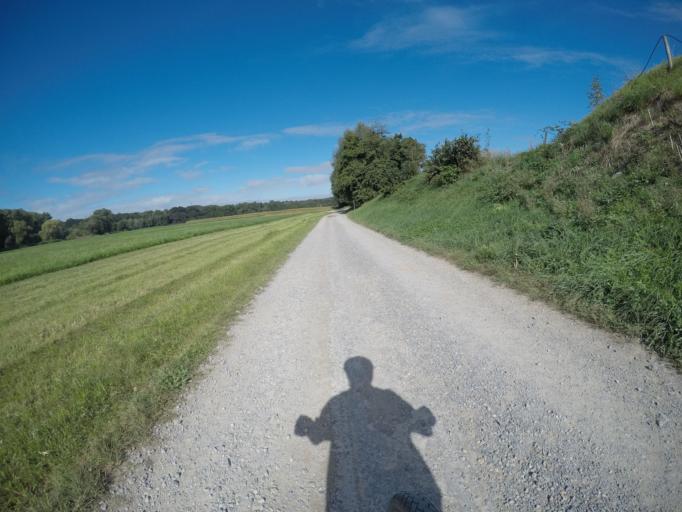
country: DE
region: Baden-Wuerttemberg
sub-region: Regierungsbezirk Stuttgart
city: Freiberg am Neckar
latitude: 48.9445
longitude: 9.1940
